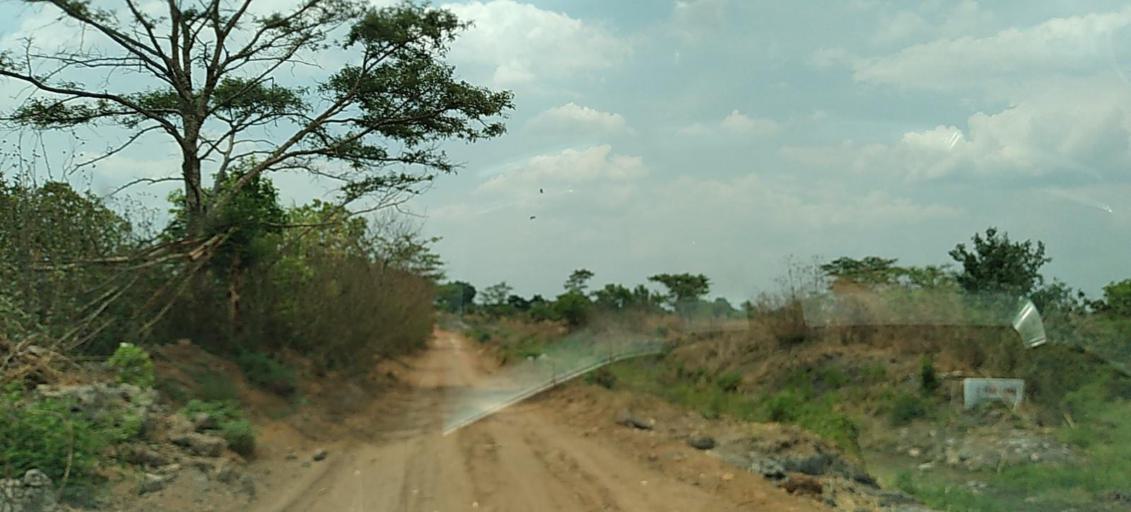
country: ZM
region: Copperbelt
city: Chililabombwe
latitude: -12.3690
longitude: 27.7998
